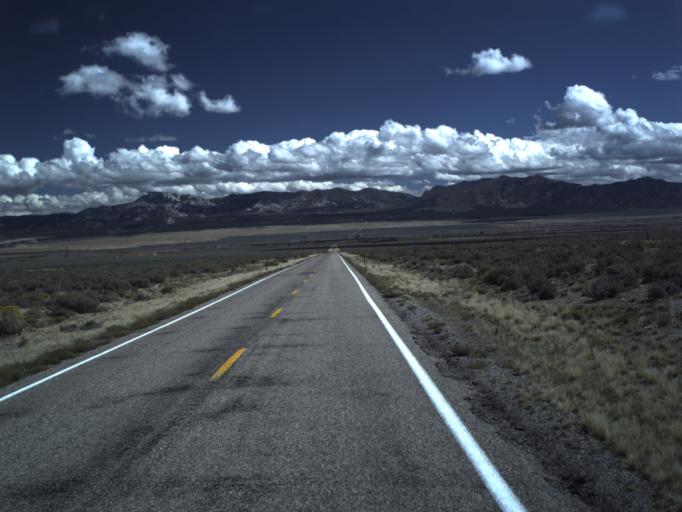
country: US
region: Utah
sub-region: Beaver County
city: Milford
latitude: 38.4196
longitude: -113.0955
